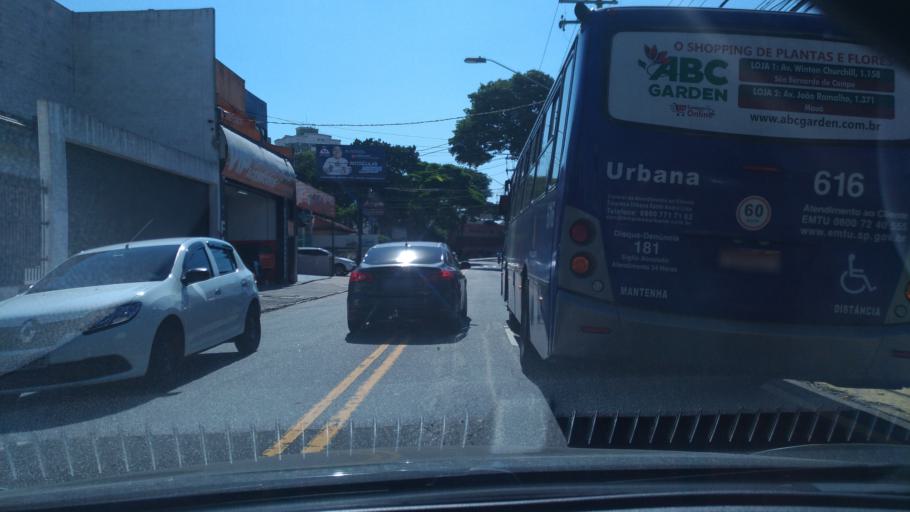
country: BR
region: Sao Paulo
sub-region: Santo Andre
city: Santo Andre
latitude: -23.6659
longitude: -46.5432
